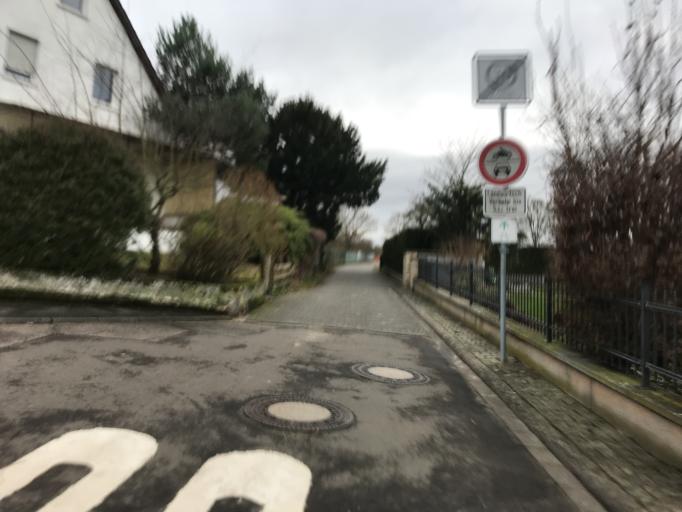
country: DE
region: Rheinland-Pfalz
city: Wackernheim
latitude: 49.9921
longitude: 8.1030
